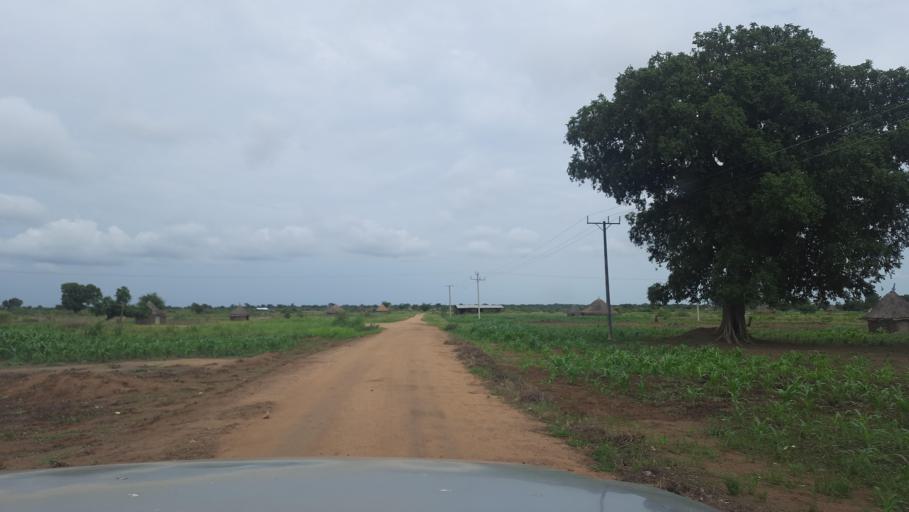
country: ET
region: Gambela
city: Gambela
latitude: 8.3278
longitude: 33.7081
